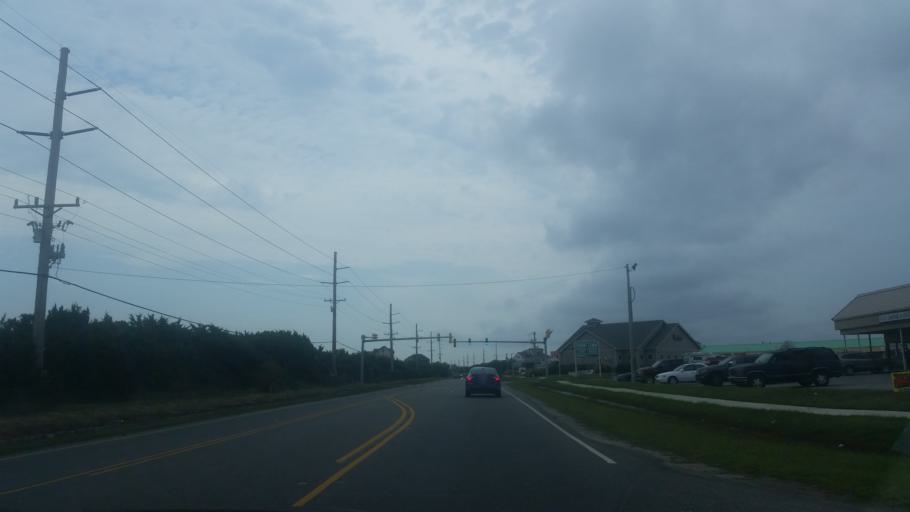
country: US
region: North Carolina
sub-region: Dare County
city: Buxton
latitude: 35.3348
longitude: -75.5066
